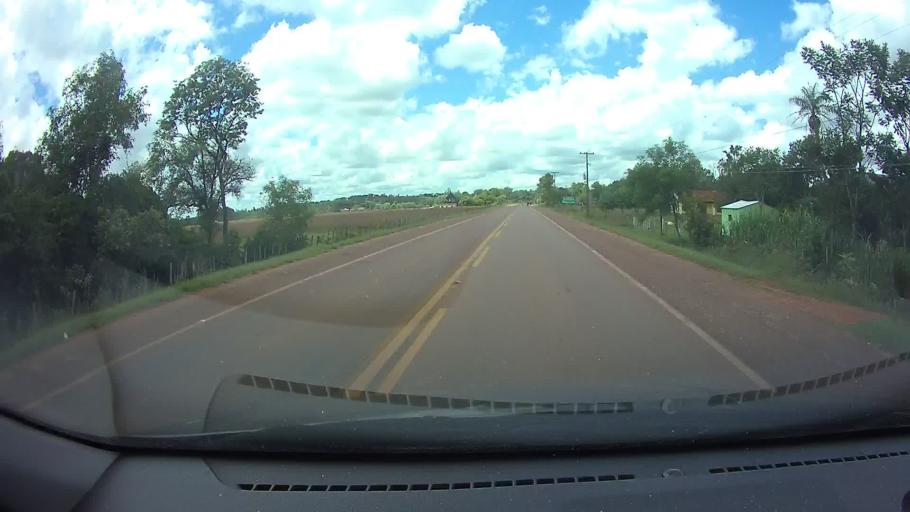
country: PY
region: Paraguari
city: La Colmena
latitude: -25.8982
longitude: -56.7960
